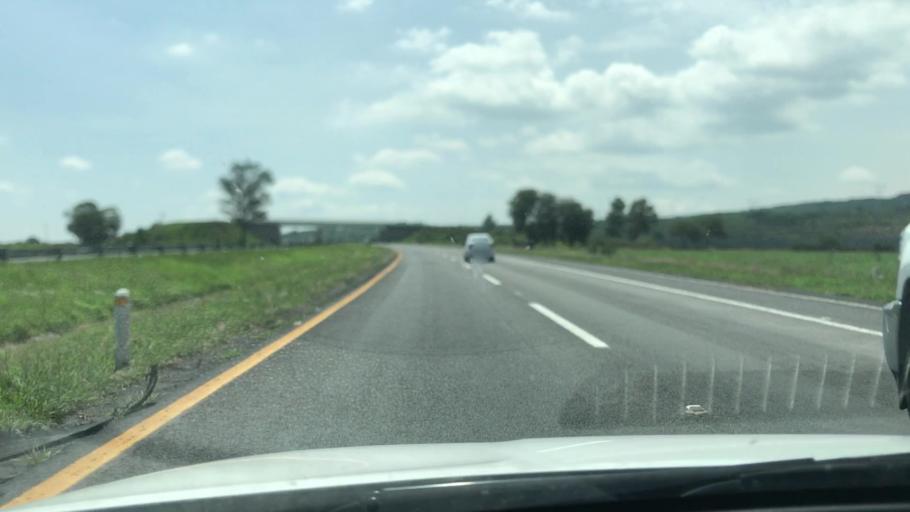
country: MX
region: Jalisco
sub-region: Poncitlan
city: Santa Cruz el Grande
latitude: 20.4426
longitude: -102.8598
